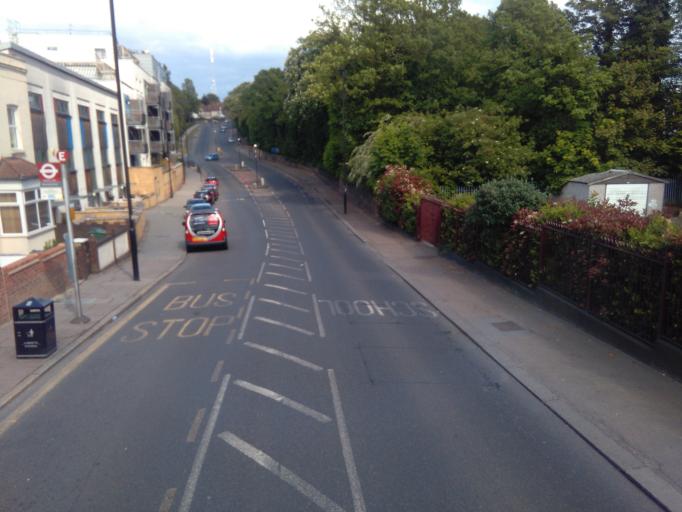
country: GB
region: England
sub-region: Greater London
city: Thornton Heath
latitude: 51.4227
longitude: -0.0989
